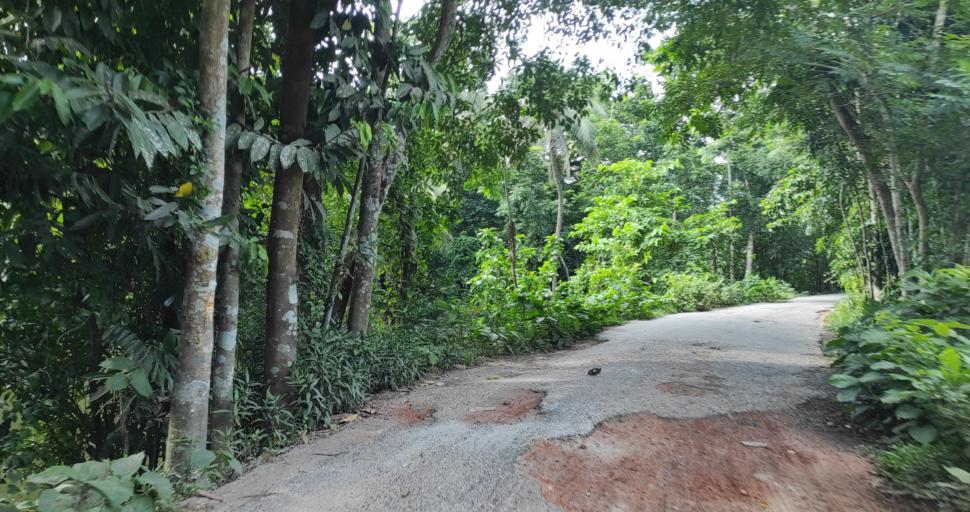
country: BD
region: Barisal
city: Gaurnadi
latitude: 22.8950
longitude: 90.1864
